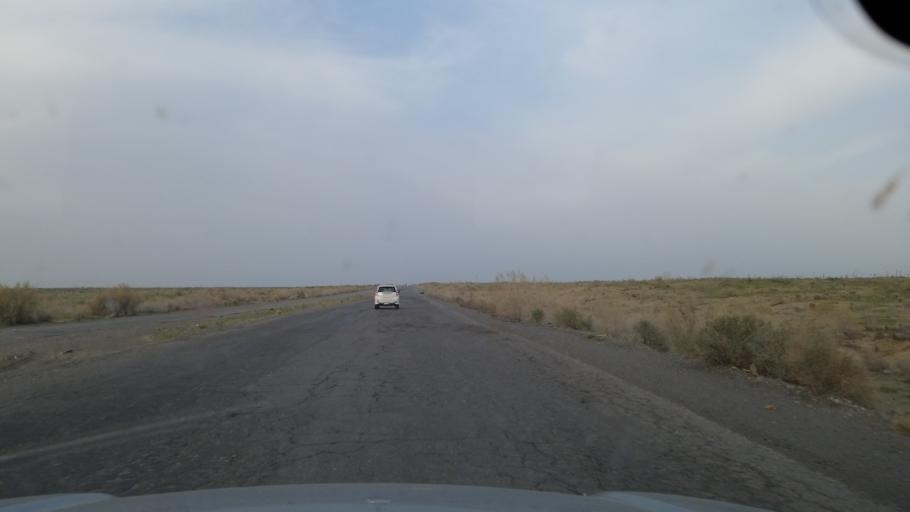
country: TM
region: Mary
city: Bayramaly
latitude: 38.2709
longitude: 62.9486
